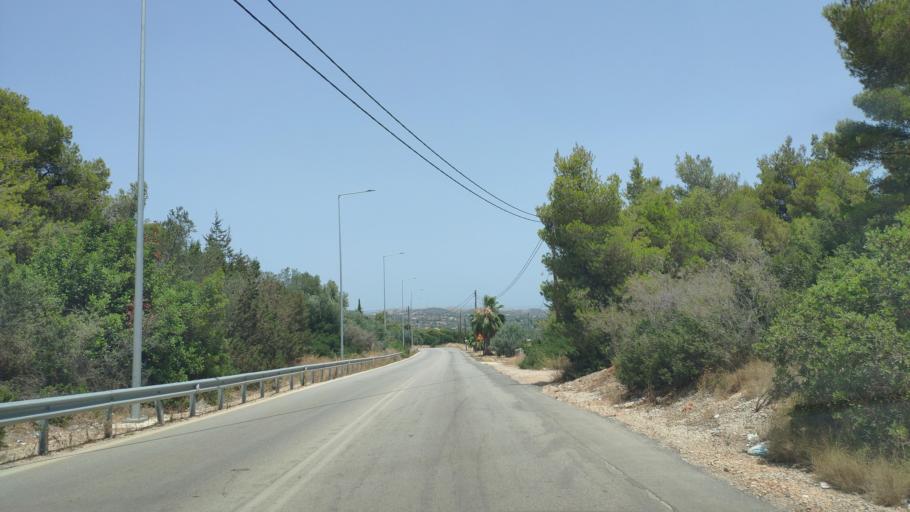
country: GR
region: Peloponnese
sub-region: Nomos Argolidos
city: Porto Cheli
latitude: 37.3358
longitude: 23.1529
